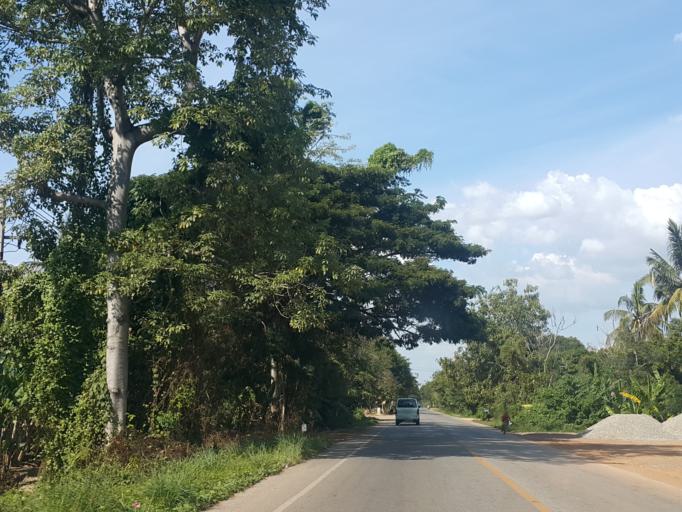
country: TH
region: Sukhothai
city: Sawankhalok
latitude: 17.2704
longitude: 99.8309
